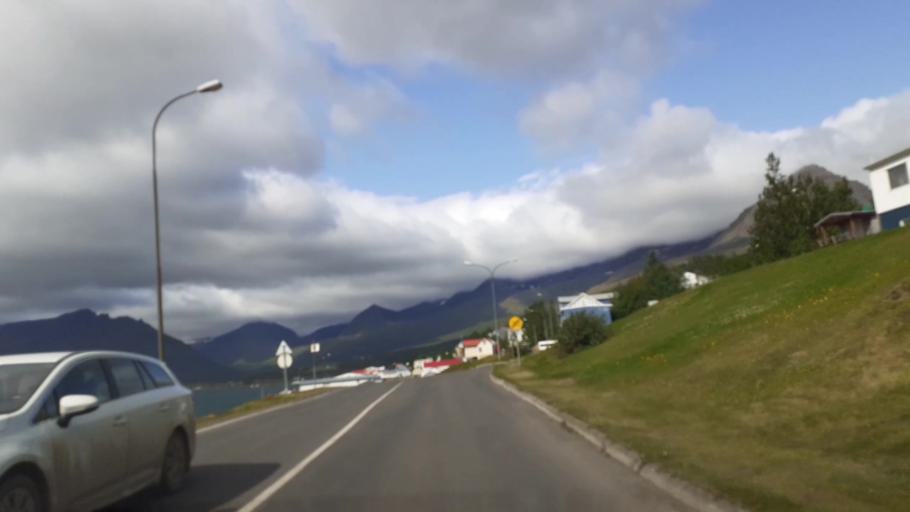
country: IS
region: East
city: Eskifjoerdur
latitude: 64.9272
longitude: -14.0034
